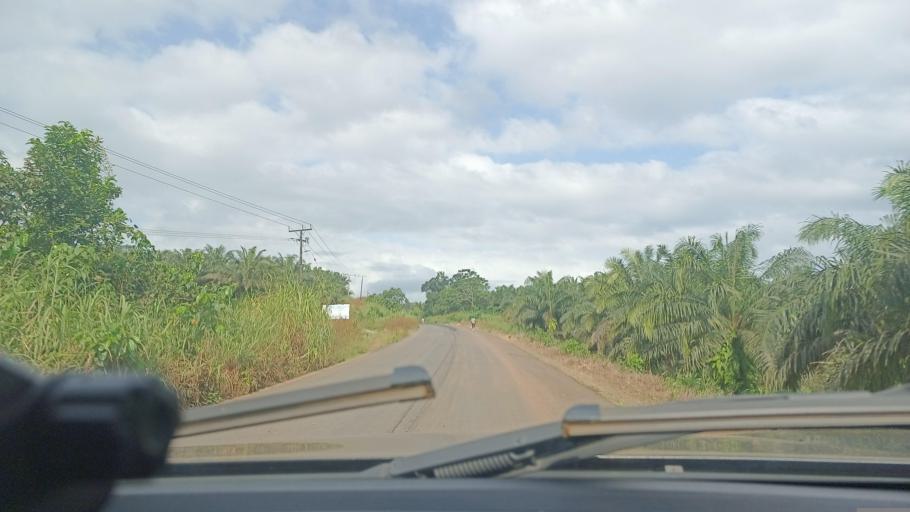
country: LR
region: Bomi
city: Tubmanburg
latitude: 6.7310
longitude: -10.9918
